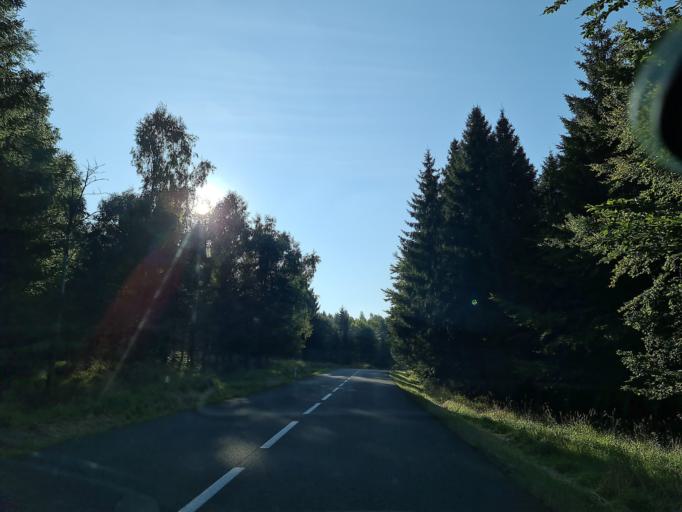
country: DE
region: Saxony
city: Deutschneudorf
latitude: 50.5903
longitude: 13.4694
